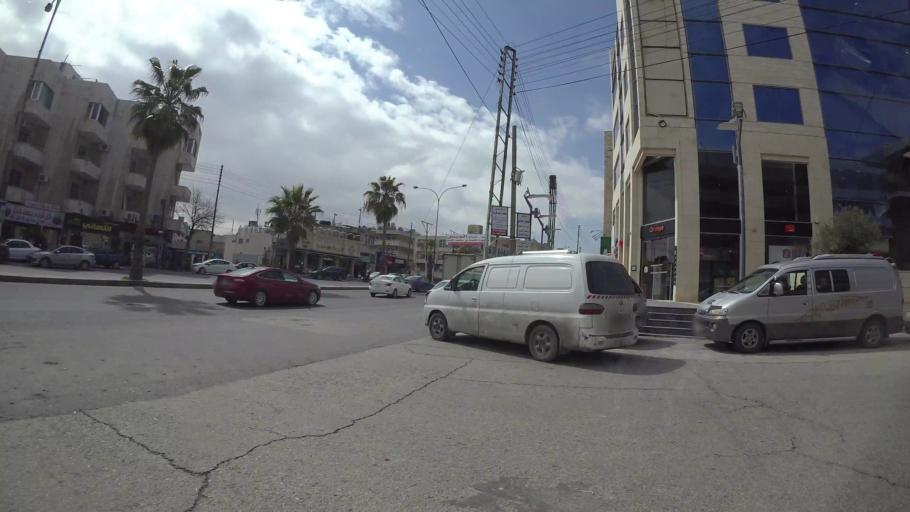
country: JO
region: Amman
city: Wadi as Sir
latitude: 31.9548
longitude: 35.8411
